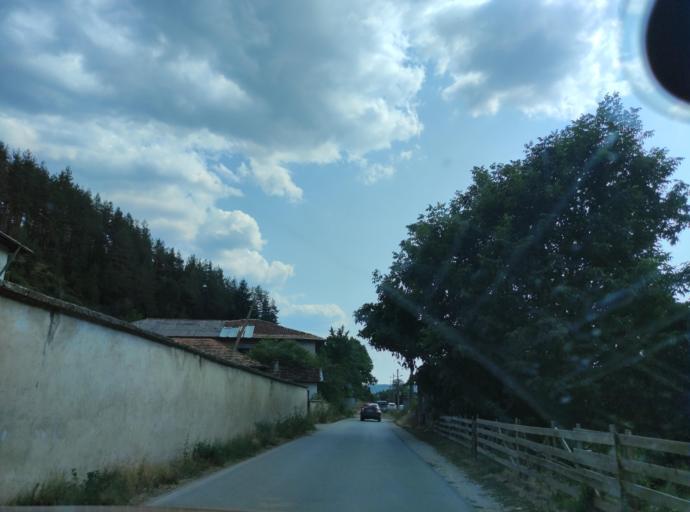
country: BG
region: Blagoevgrad
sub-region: Obshtina Belitsa
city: Belitsa
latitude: 41.9565
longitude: 23.5568
